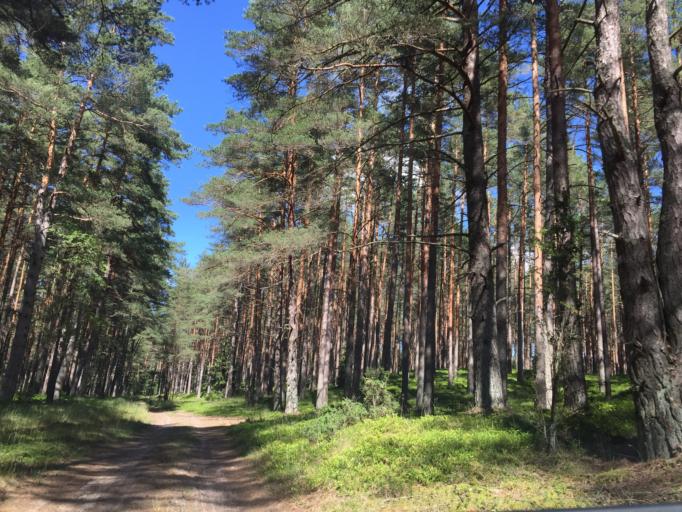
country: LV
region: Ventspils
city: Ventspils
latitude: 57.4694
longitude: 21.6413
